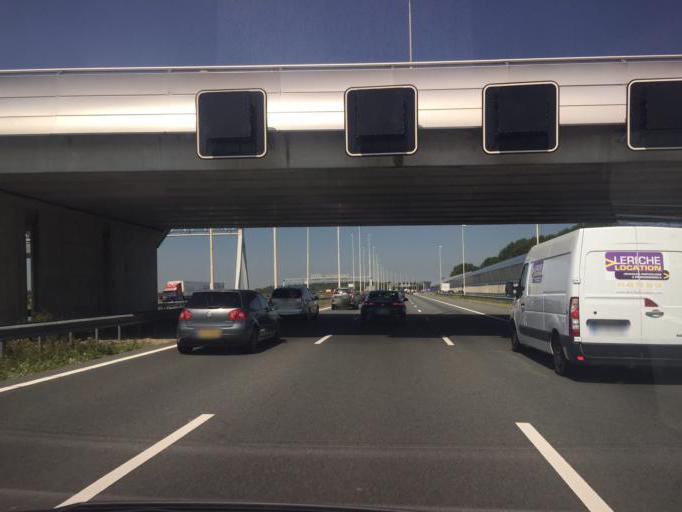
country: NL
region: Utrecht
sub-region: Stichtse Vecht
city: Spechtenkamp
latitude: 52.1244
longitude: 5.0216
